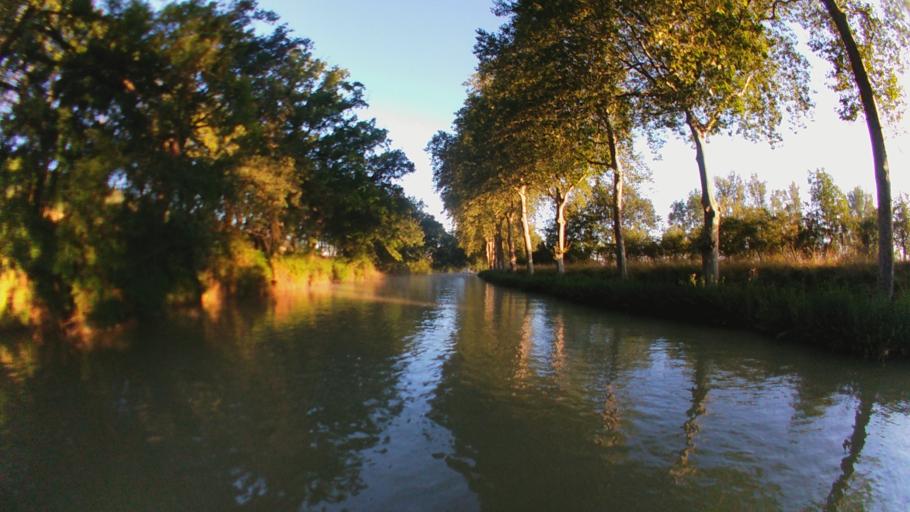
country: FR
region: Midi-Pyrenees
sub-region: Departement de la Haute-Garonne
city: Gardouch
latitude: 43.4036
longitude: 1.6687
